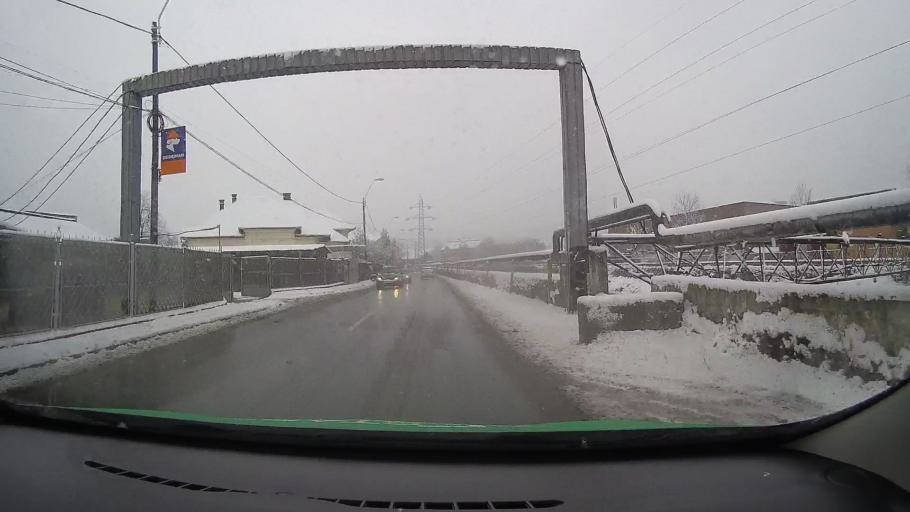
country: RO
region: Hunedoara
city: Hunedoara
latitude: 45.7542
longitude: 22.8953
